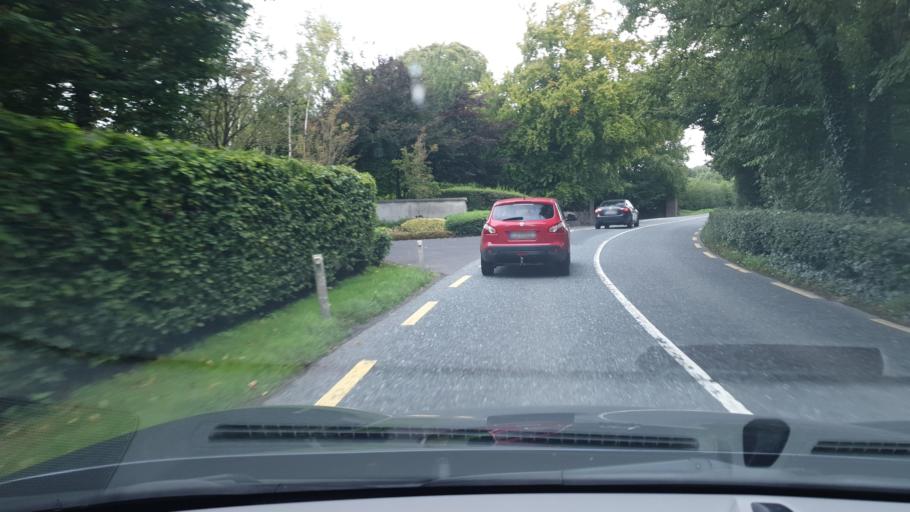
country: IE
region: Leinster
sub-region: Kildare
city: Clane
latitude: 53.2684
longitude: -6.6888
